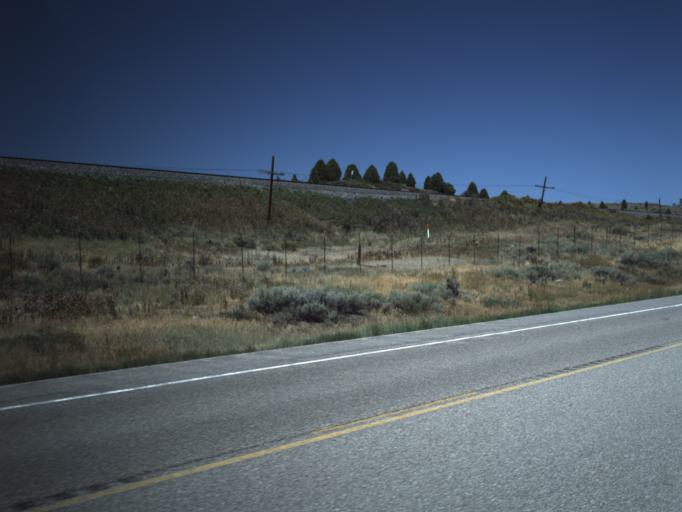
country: US
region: Utah
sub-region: Carbon County
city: Helper
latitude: 39.9057
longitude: -111.0594
